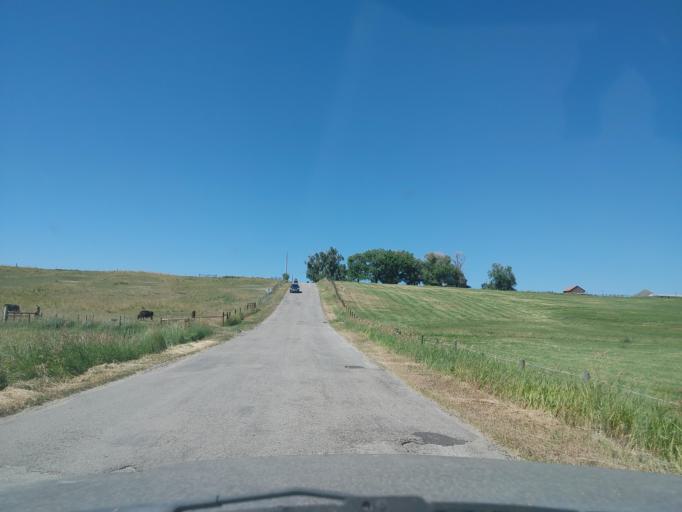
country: US
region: Montana
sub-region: Ravalli County
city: Hamilton
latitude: 46.3140
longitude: -114.0612
